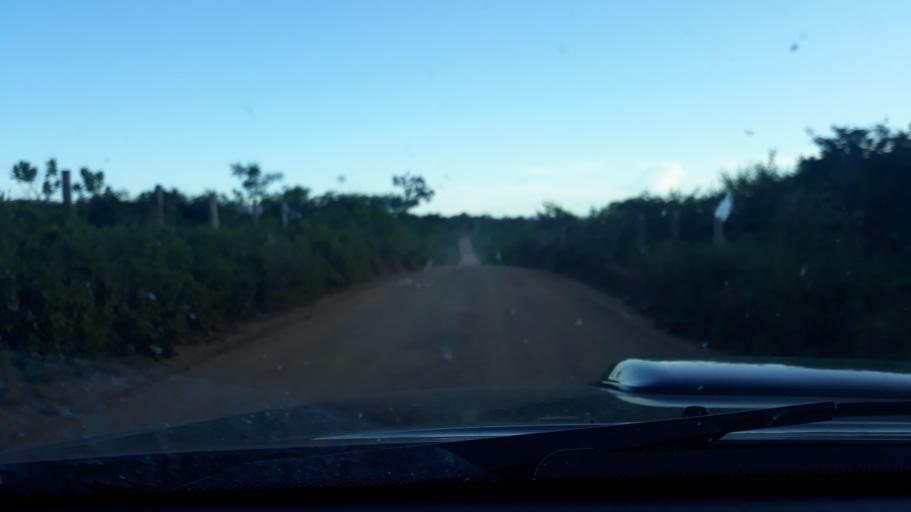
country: BR
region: Bahia
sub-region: Riacho De Santana
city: Riacho de Santana
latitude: -13.8012
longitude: -42.7127
